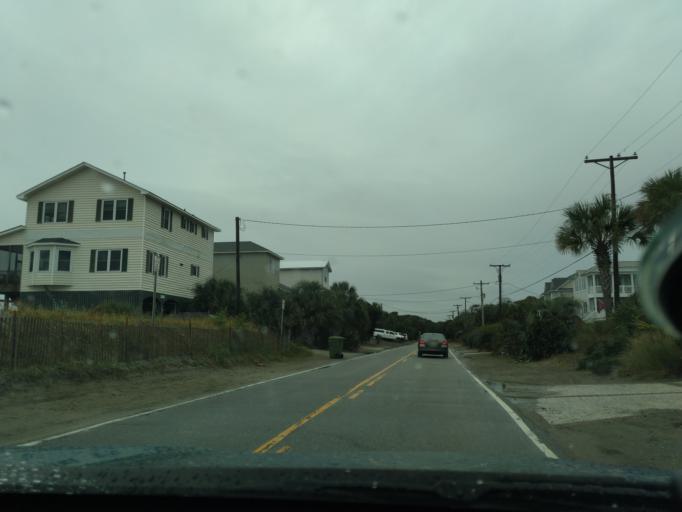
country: US
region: South Carolina
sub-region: Charleston County
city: Folly Beach
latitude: 32.6681
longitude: -79.9107
